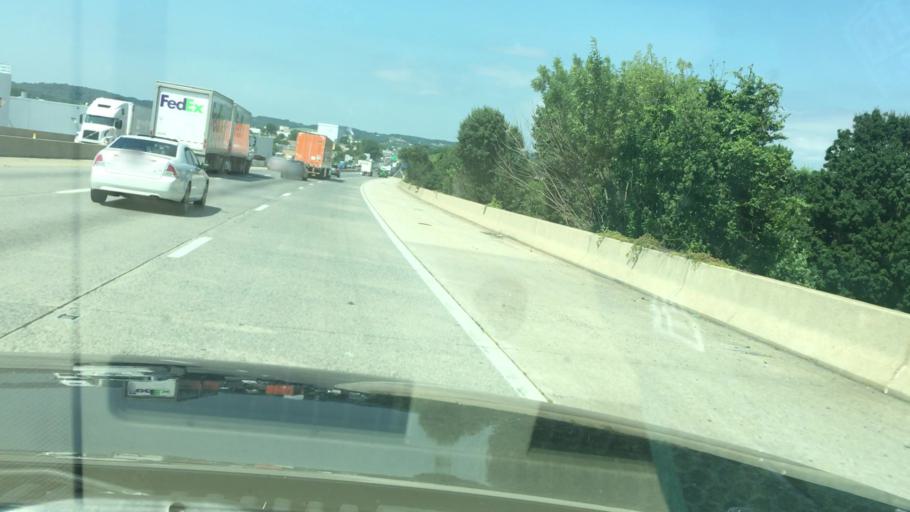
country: US
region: Pennsylvania
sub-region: Lehigh County
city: Trexlertown
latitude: 40.5837
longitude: -75.6047
